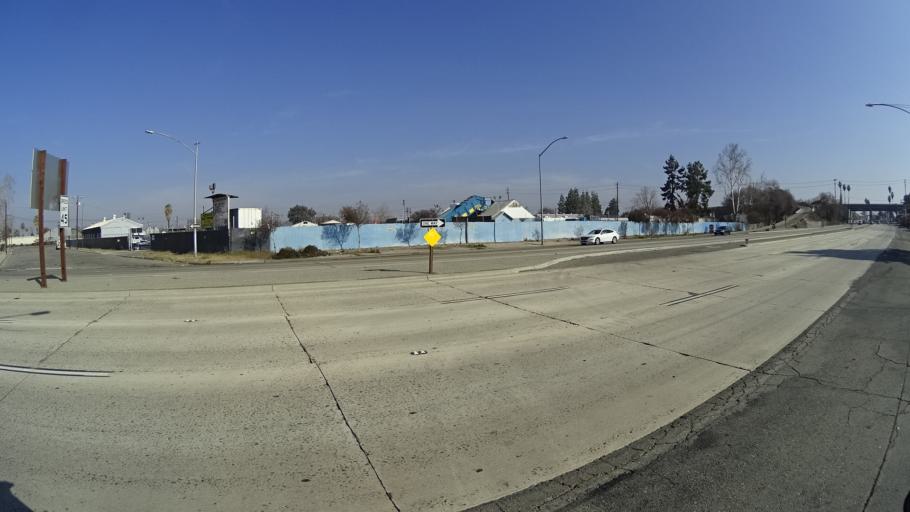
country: US
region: California
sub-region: Kern County
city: Bakersfield
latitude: 35.3834
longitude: -119.0132
